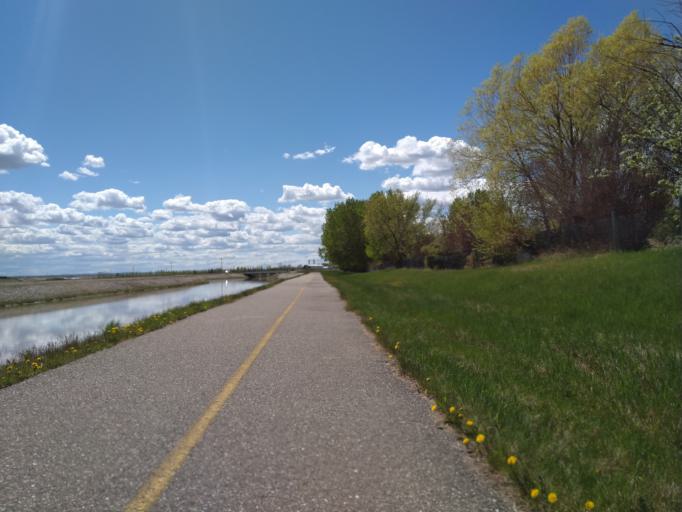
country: CA
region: Alberta
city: Chestermere
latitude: 50.9914
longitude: -113.8635
